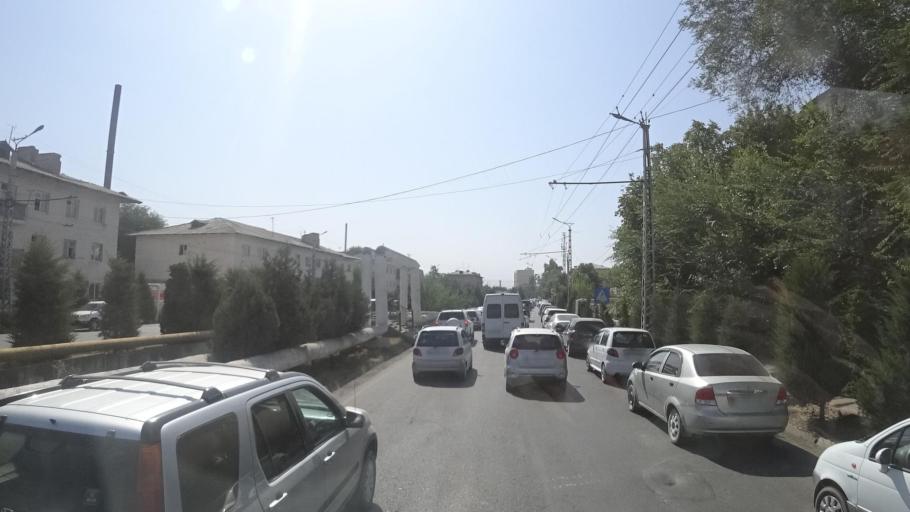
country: KG
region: Osh
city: Osh
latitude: 40.5205
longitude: 72.8092
